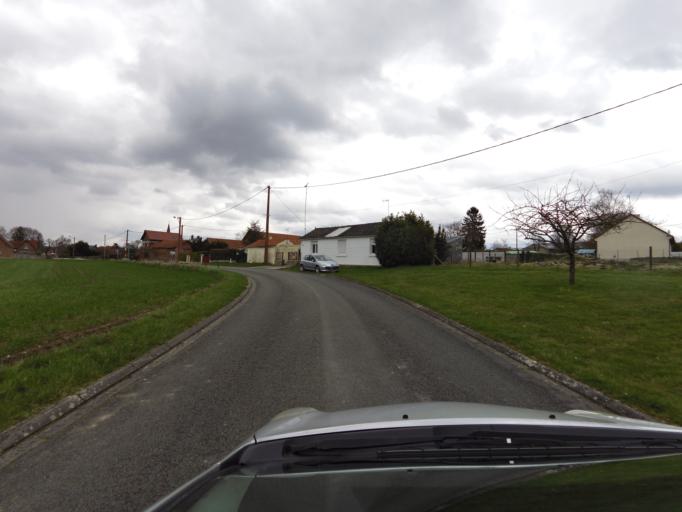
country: FR
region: Picardie
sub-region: Departement de la Somme
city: Bray-sur-Somme
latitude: 49.9388
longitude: 2.8173
